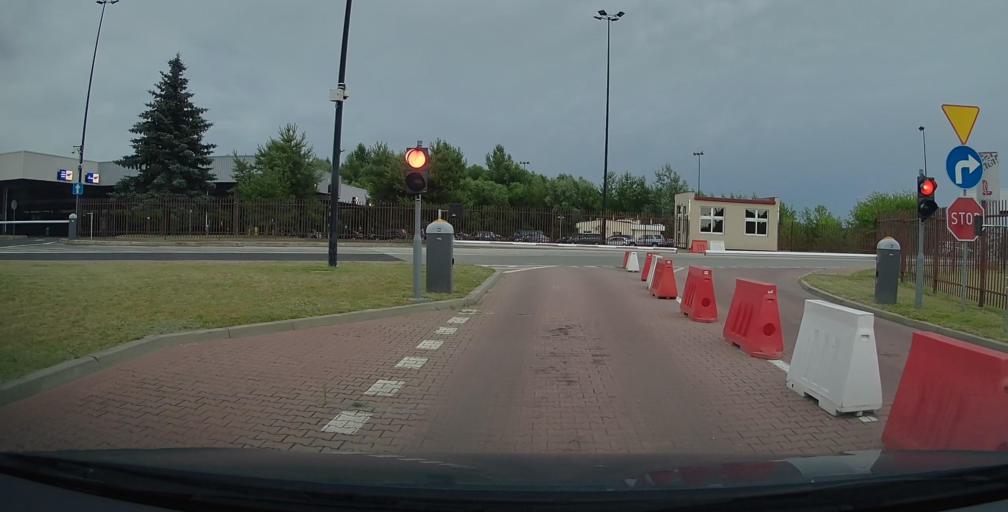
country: PL
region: Lublin Voivodeship
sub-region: Powiat bialski
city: Terespol
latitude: 52.0704
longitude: 23.6422
